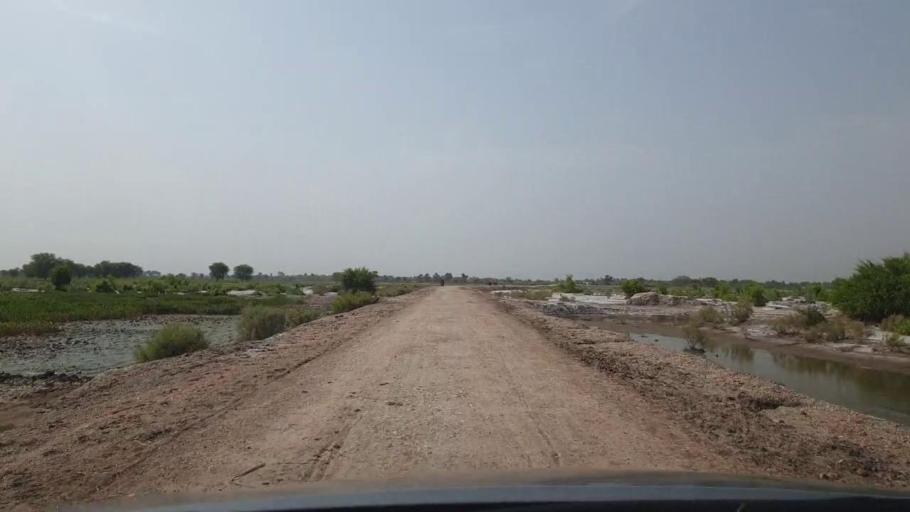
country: PK
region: Sindh
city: Rohri
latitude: 27.6703
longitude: 69.0134
